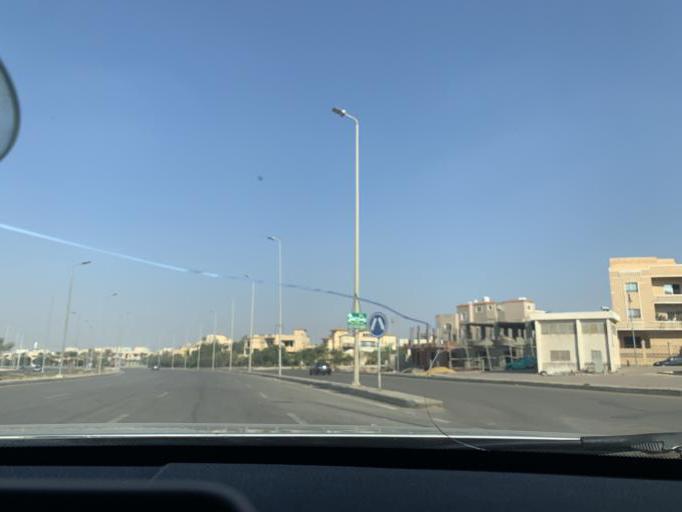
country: EG
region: Muhafazat al Qalyubiyah
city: Al Khankah
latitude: 30.0088
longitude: 31.4726
